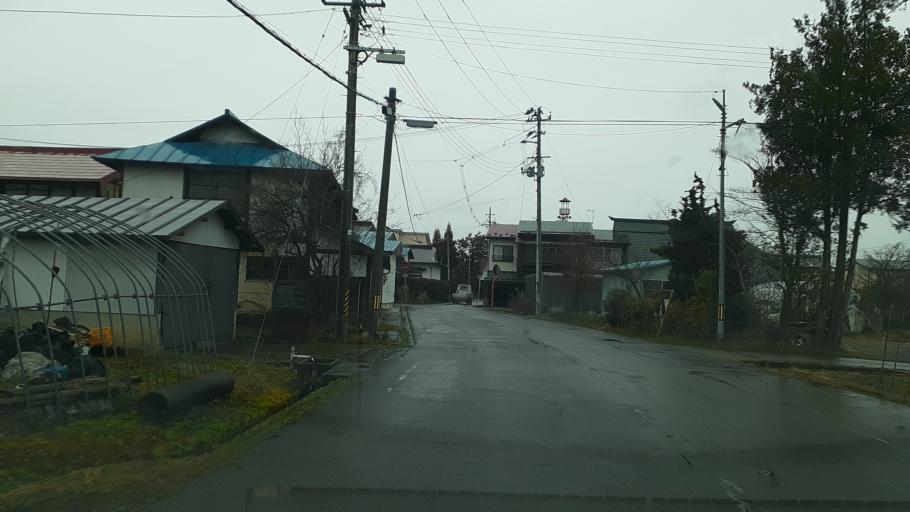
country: JP
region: Fukushima
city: Kitakata
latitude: 37.5832
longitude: 139.8542
